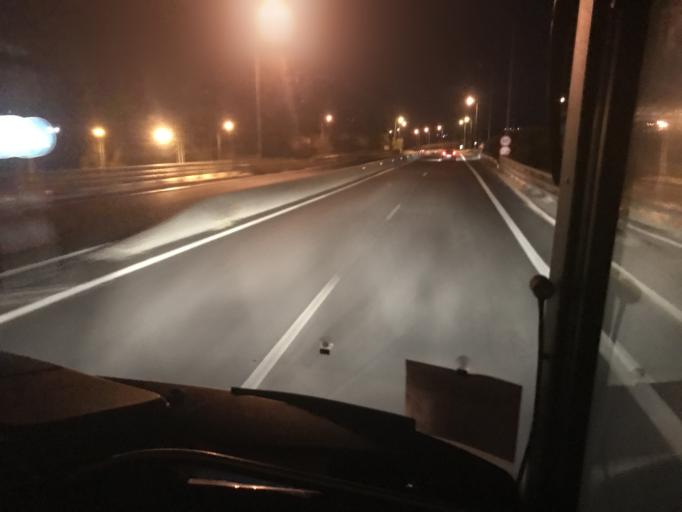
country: GR
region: Crete
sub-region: Nomos Irakleiou
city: Skalanion
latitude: 35.2638
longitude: 25.1825
